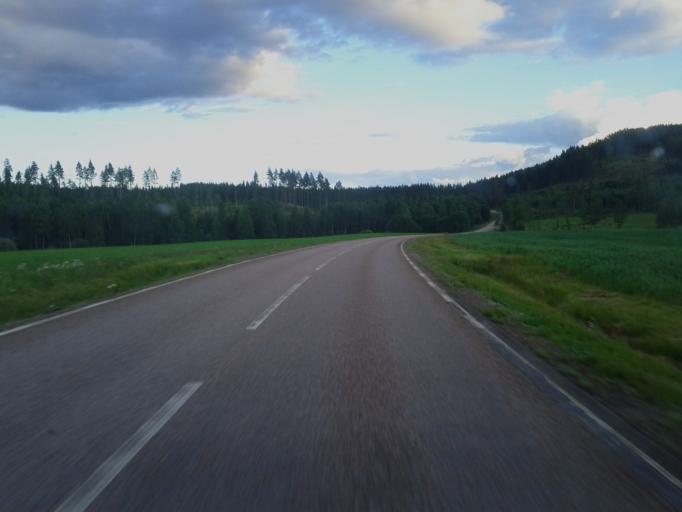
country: SE
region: Dalarna
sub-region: Borlange Kommun
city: Borlaenge
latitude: 60.3758
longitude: 15.3855
